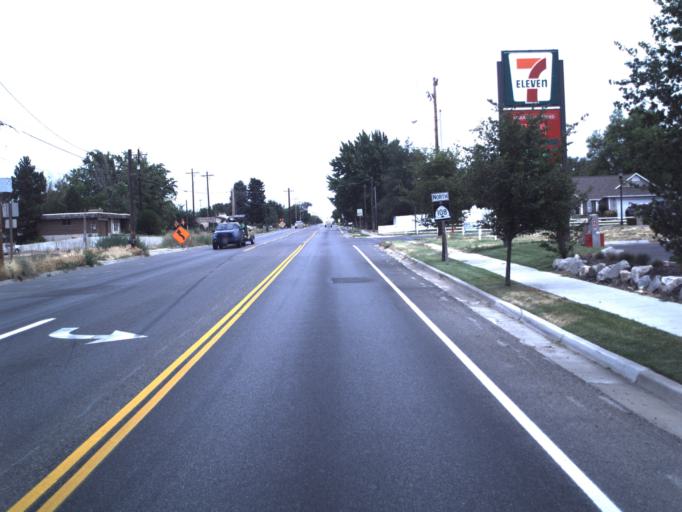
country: US
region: Utah
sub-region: Davis County
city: West Point
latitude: 41.1183
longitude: -112.0645
